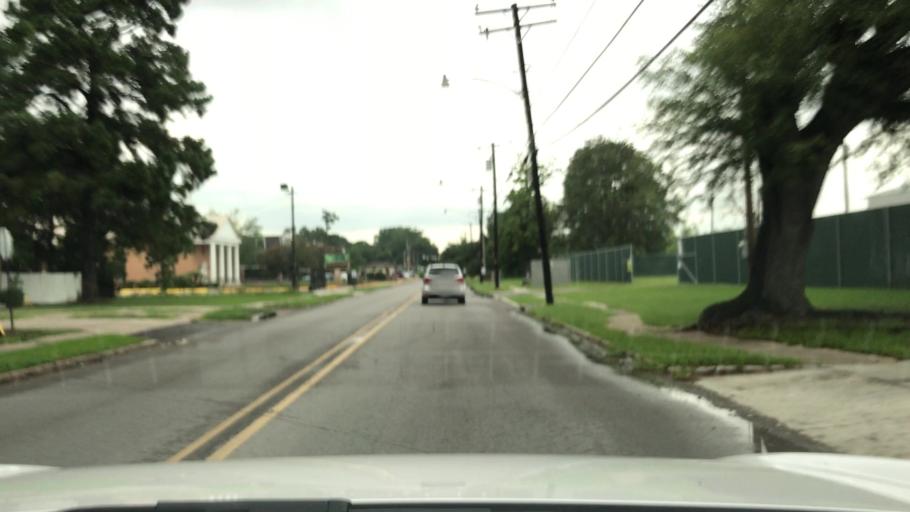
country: US
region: Louisiana
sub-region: East Baton Rouge Parish
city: Merrydale
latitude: 30.4773
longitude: -91.1175
